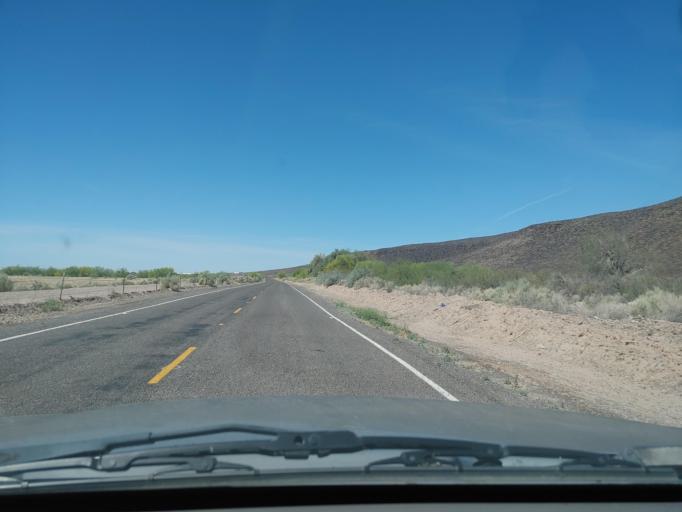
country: US
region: Arizona
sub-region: Maricopa County
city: Gila Bend
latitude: 32.9863
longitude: -113.3126
